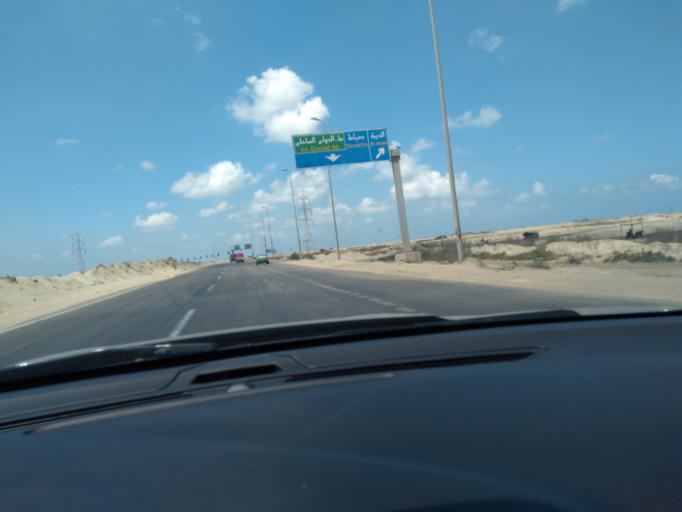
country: EG
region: Muhafazat ad Daqahliyah
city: Al Matariyah
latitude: 31.3504
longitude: 32.0541
